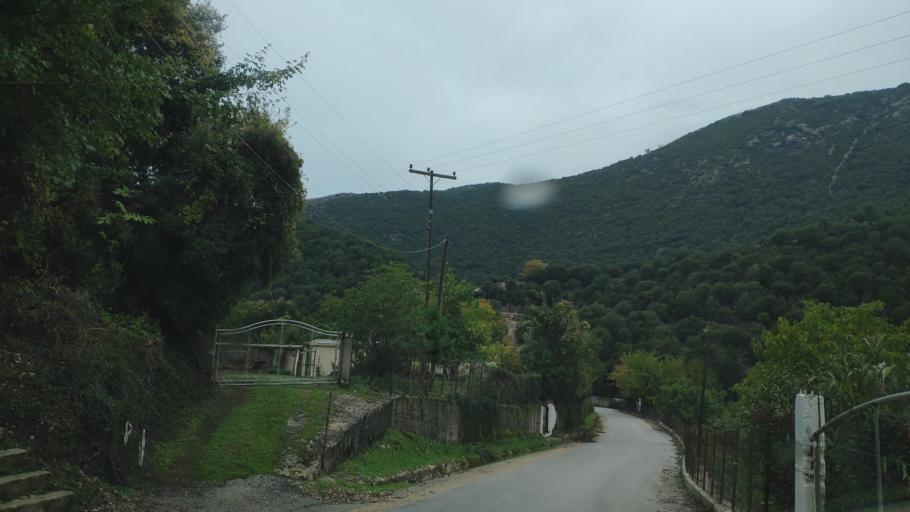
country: GR
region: Epirus
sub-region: Nomos Thesprotias
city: Paramythia
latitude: 39.4323
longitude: 20.6270
